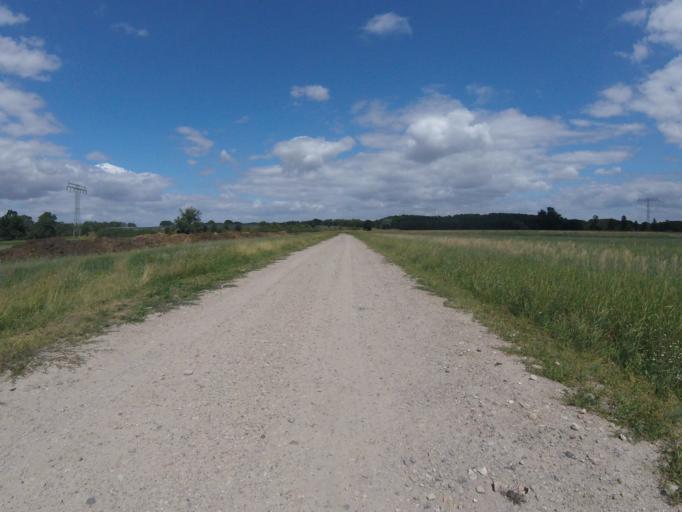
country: DE
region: Brandenburg
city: Mittenwalde
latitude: 52.2474
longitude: 13.5341
